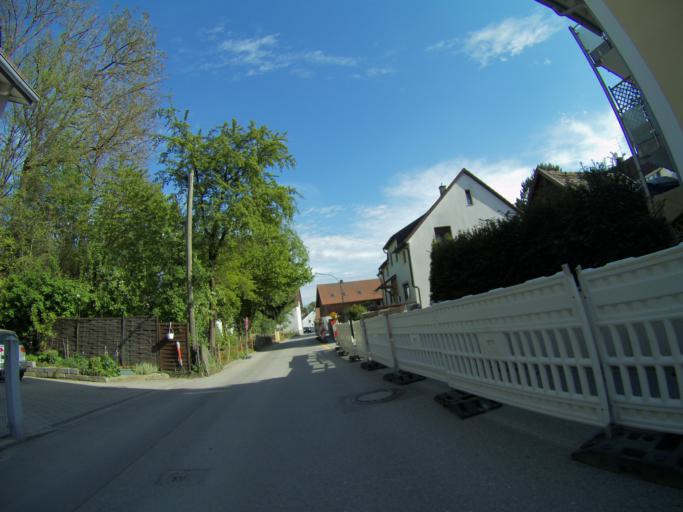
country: DE
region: Bavaria
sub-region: Upper Bavaria
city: Freising
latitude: 48.3972
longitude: 11.7176
